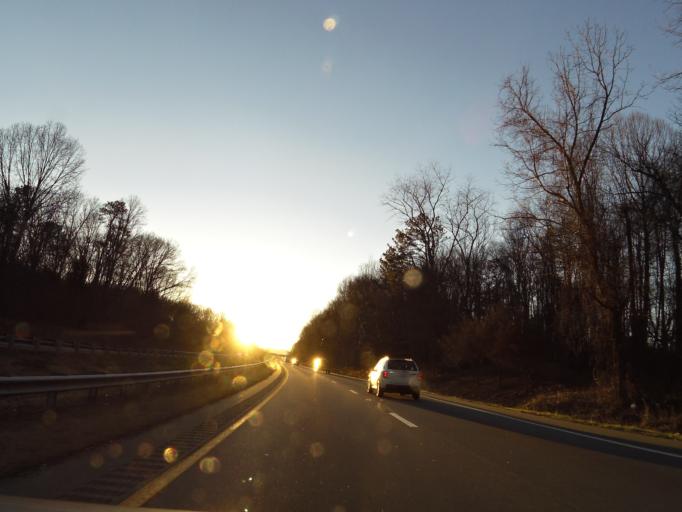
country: US
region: North Carolina
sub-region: Buncombe County
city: Bent Creek
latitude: 35.5578
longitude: -82.6678
